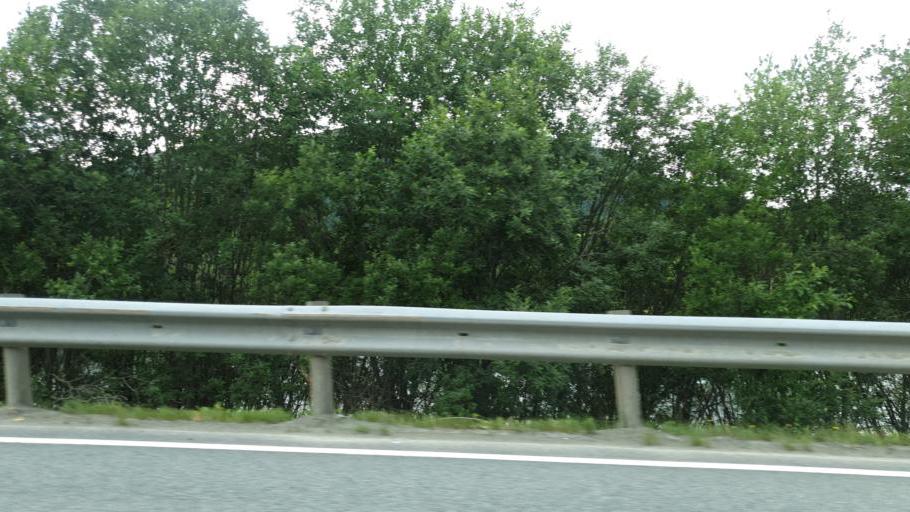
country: NO
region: Sor-Trondelag
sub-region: Oppdal
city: Oppdal
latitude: 62.5522
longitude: 9.6325
